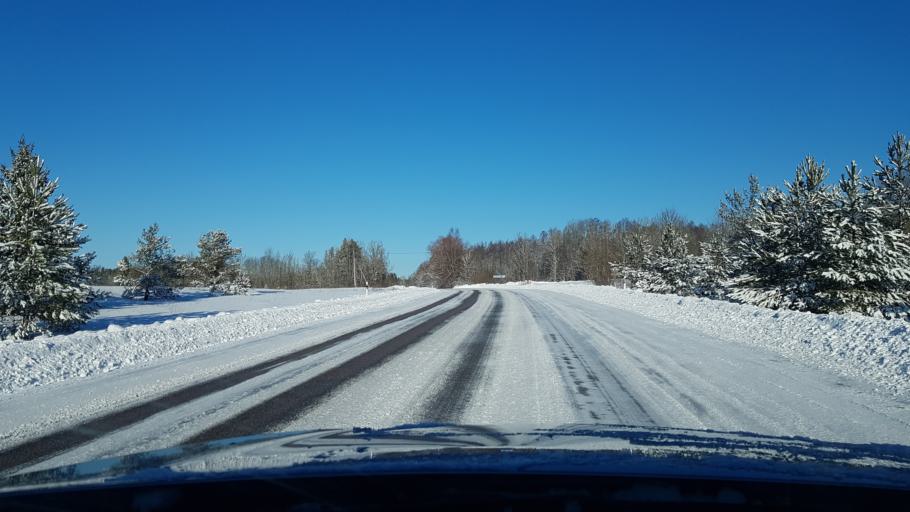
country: EE
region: Hiiumaa
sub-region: Kaerdla linn
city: Kardla
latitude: 58.9166
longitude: 22.7942
